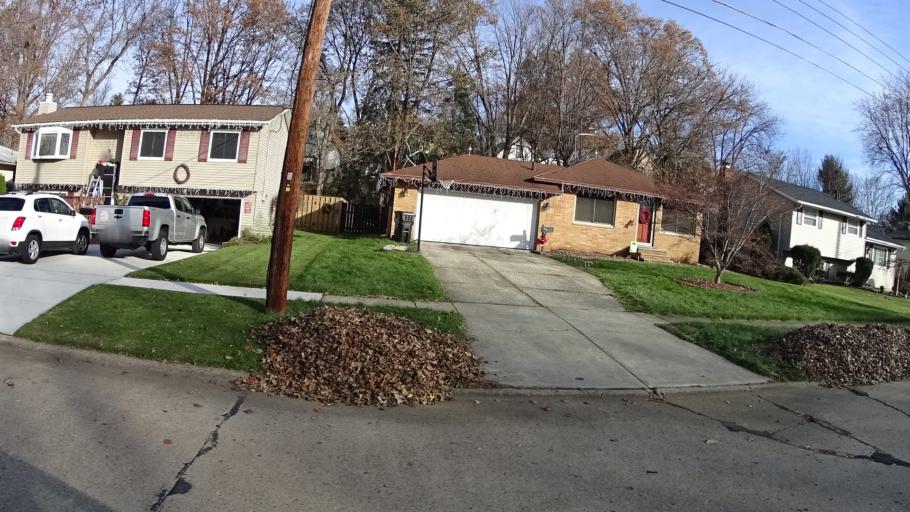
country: US
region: Ohio
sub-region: Lorain County
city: Elyria
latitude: 41.3557
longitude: -82.1011
